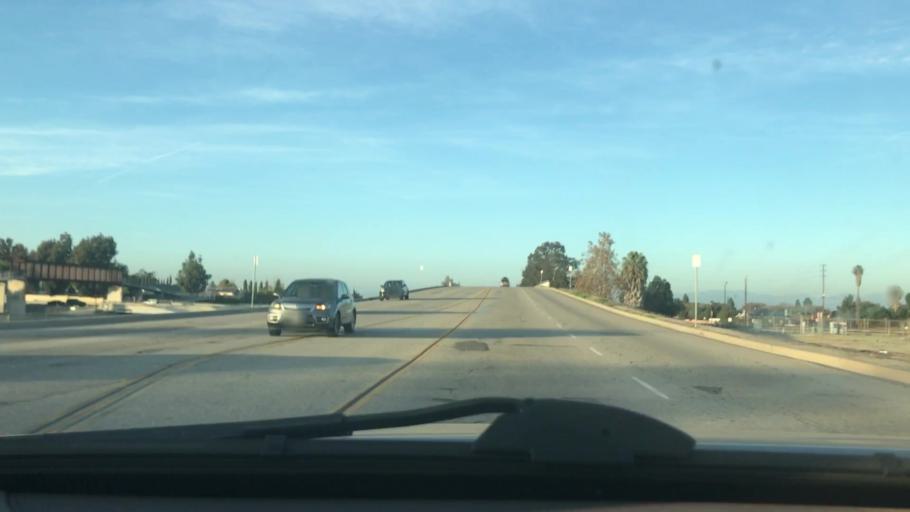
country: US
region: California
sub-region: Orange County
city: Rossmoor
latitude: 33.7725
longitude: -118.1031
